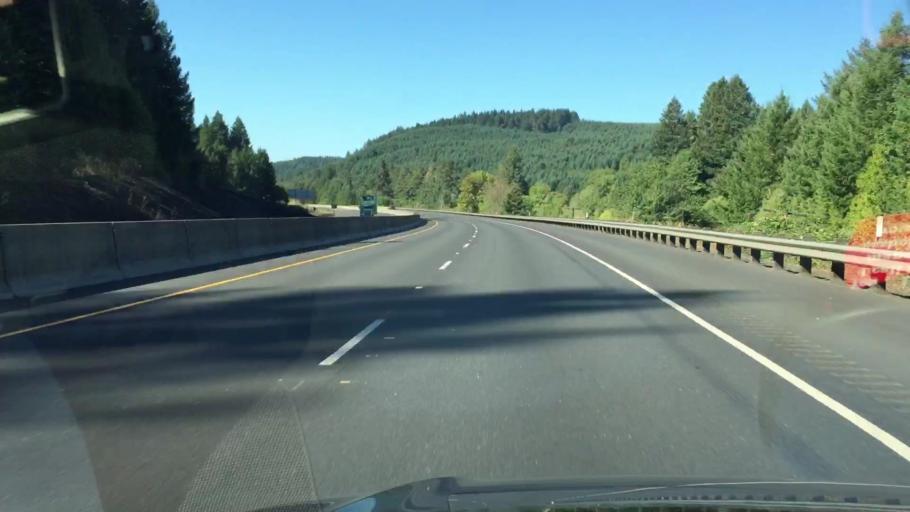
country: US
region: Oregon
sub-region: Lane County
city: Cottage Grove
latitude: 43.7399
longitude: -123.1862
